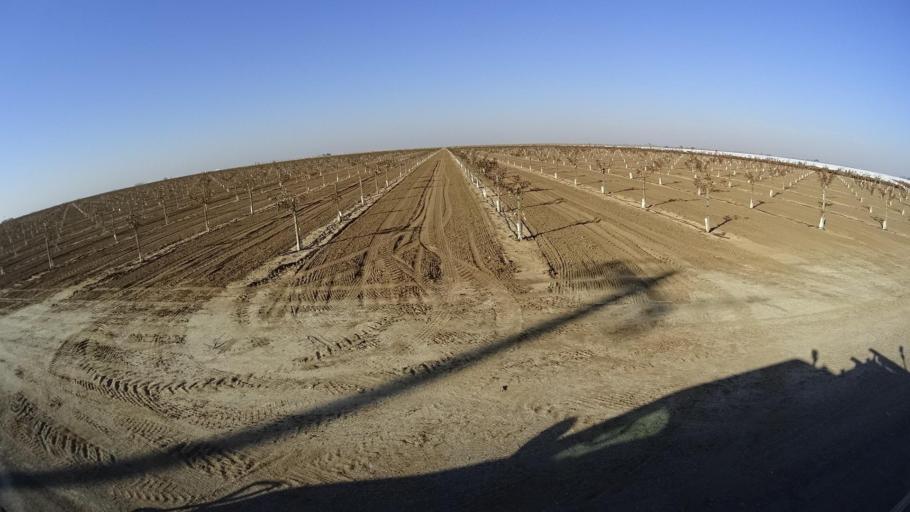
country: US
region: California
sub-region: Kern County
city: McFarland
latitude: 35.7316
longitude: -119.1695
